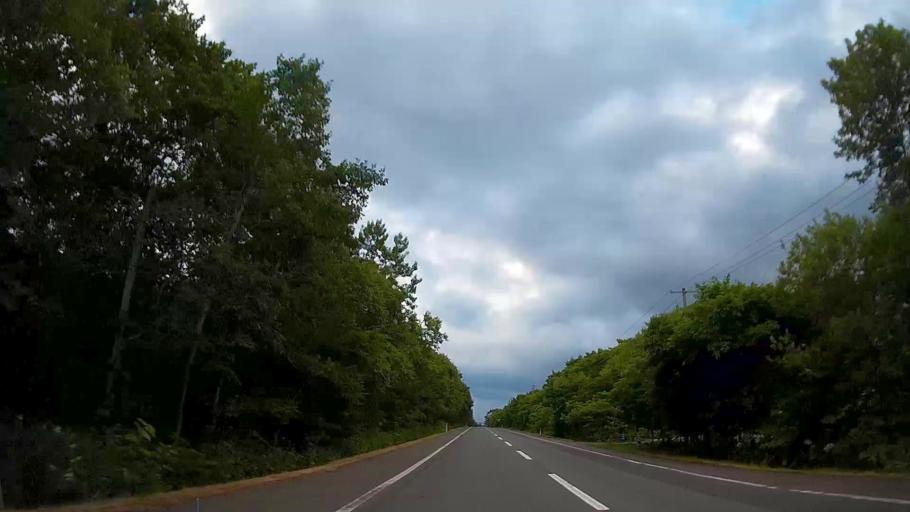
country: JP
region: Hokkaido
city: Nanae
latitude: 42.0716
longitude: 140.7830
